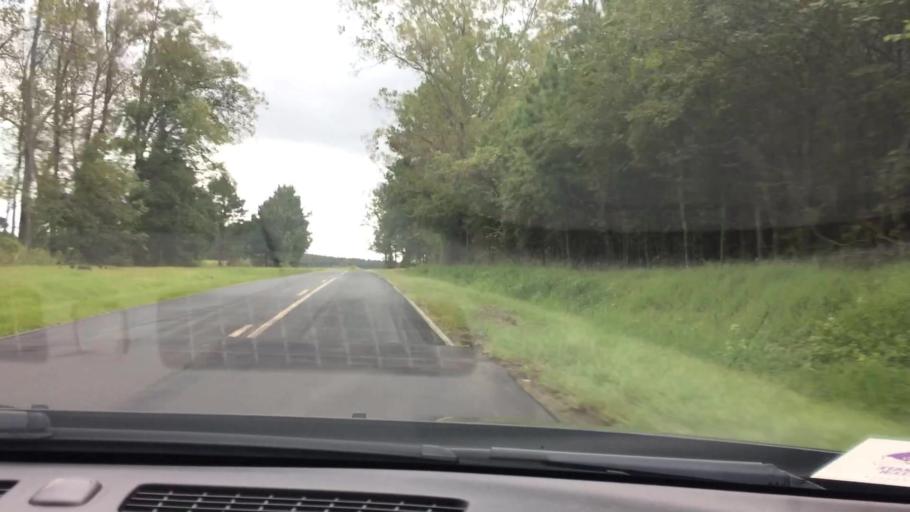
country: US
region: North Carolina
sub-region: Greene County
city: Maury
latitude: 35.5249
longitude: -77.5429
